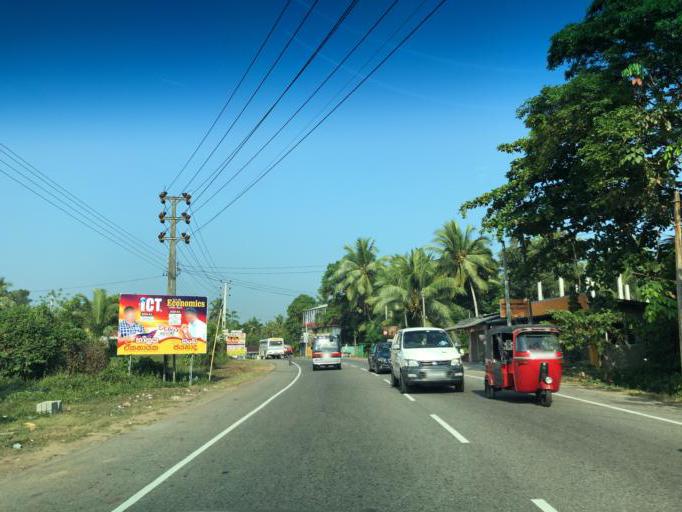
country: LK
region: Western
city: Horana South
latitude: 6.7243
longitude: 80.0871
